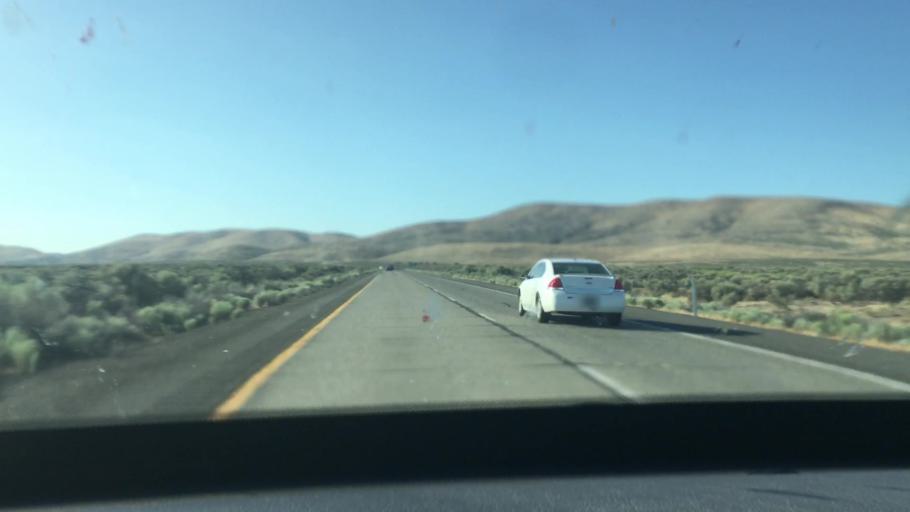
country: US
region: Washington
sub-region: Kittitas County
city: Kittitas
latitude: 46.8328
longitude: -120.3660
